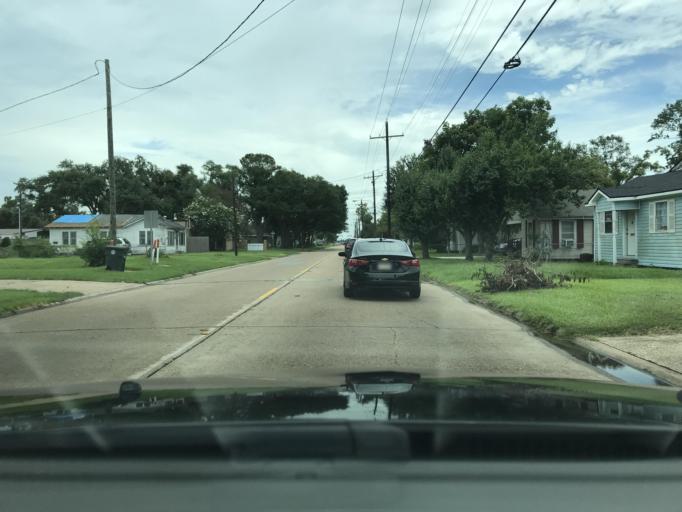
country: US
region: Louisiana
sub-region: Calcasieu Parish
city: Lake Charles
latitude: 30.2034
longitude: -93.2085
